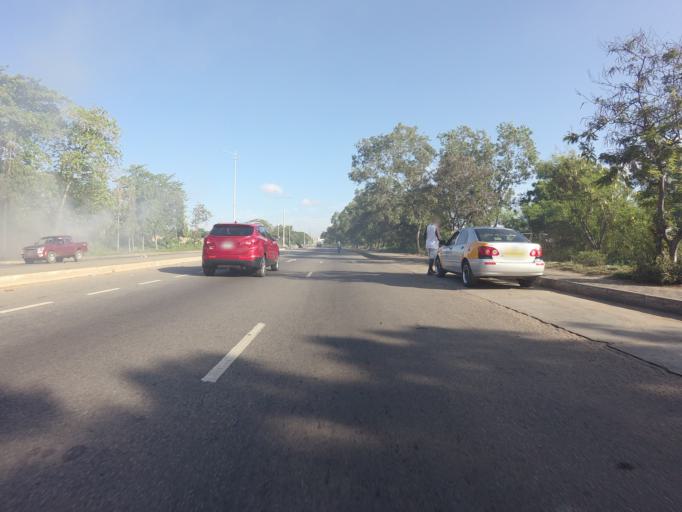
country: GH
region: Greater Accra
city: Accra
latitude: 5.5432
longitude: -0.2264
